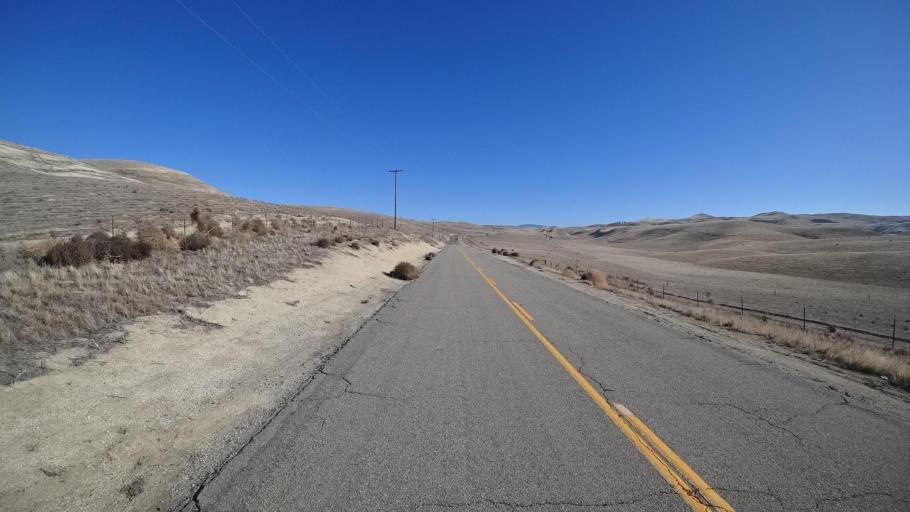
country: US
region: California
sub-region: Kern County
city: Maricopa
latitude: 34.9532
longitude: -119.4297
